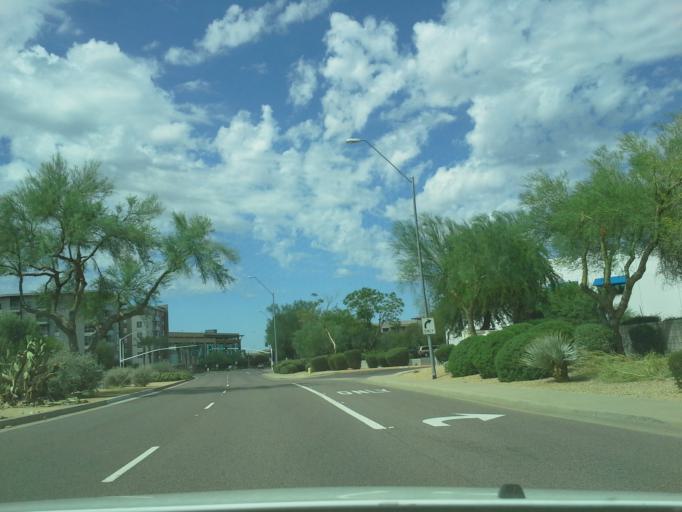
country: US
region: Arizona
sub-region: Maricopa County
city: Paradise Valley
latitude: 33.6272
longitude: -111.9207
